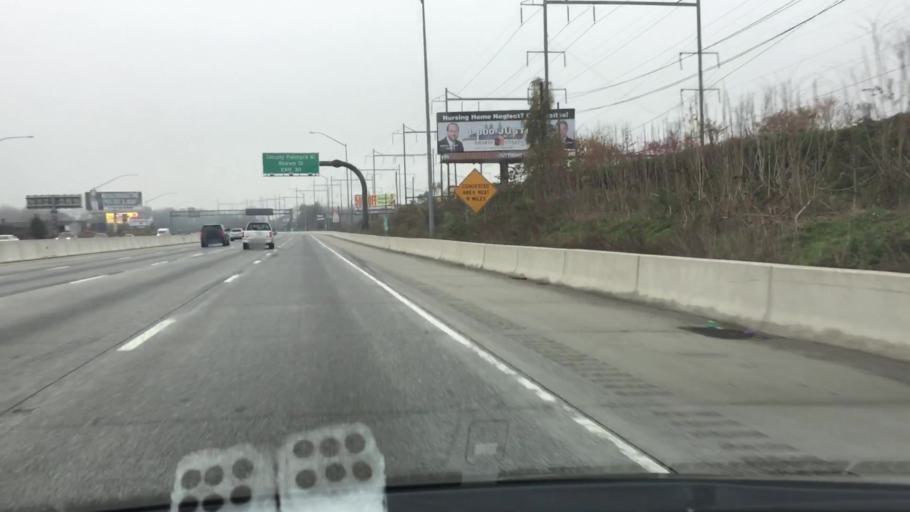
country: US
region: New Jersey
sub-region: Burlington County
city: Riverton
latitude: 40.0394
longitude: -75.0060
